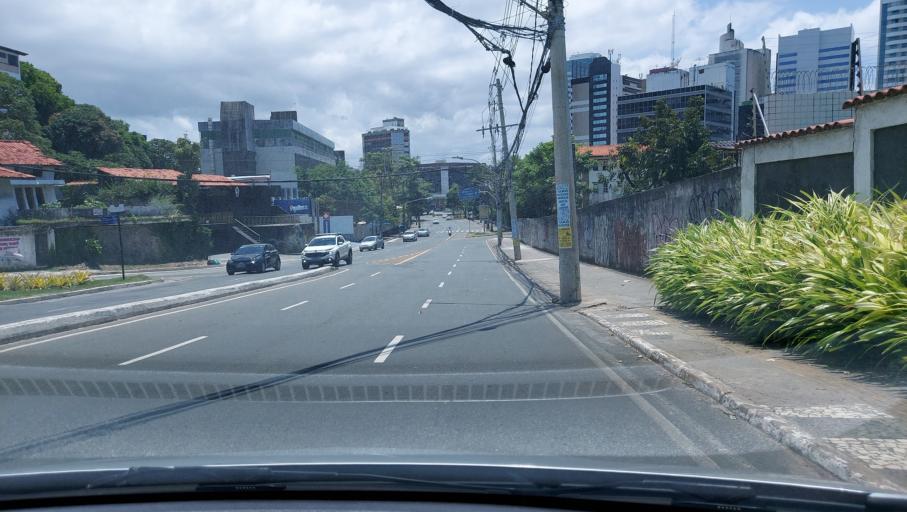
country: BR
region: Bahia
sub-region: Salvador
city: Salvador
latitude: -12.9816
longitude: -38.4585
